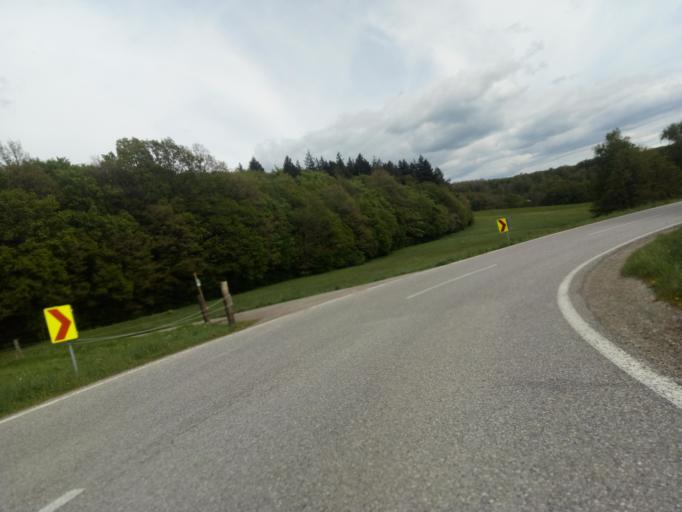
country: AT
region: Lower Austria
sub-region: Politischer Bezirk Modling
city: Breitenfurt bei Wien
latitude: 48.1258
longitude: 16.1225
